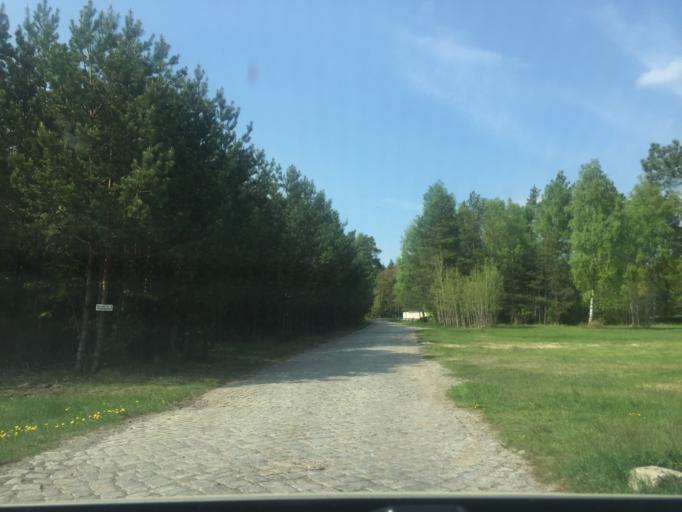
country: DE
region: Mecklenburg-Vorpommern
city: Torgelow
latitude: 53.6264
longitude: 13.9879
